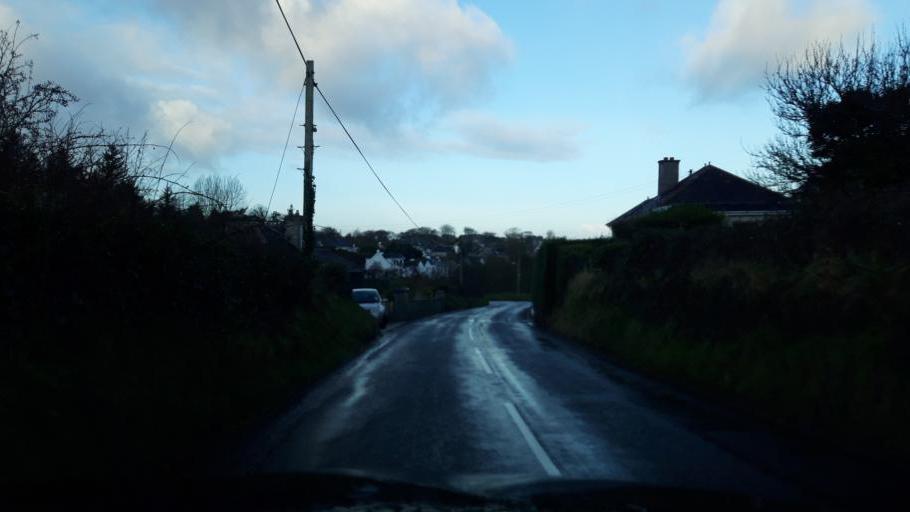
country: GB
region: Northern Ireland
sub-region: Moyle District
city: Ballycastle
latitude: 55.1982
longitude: -6.2307
